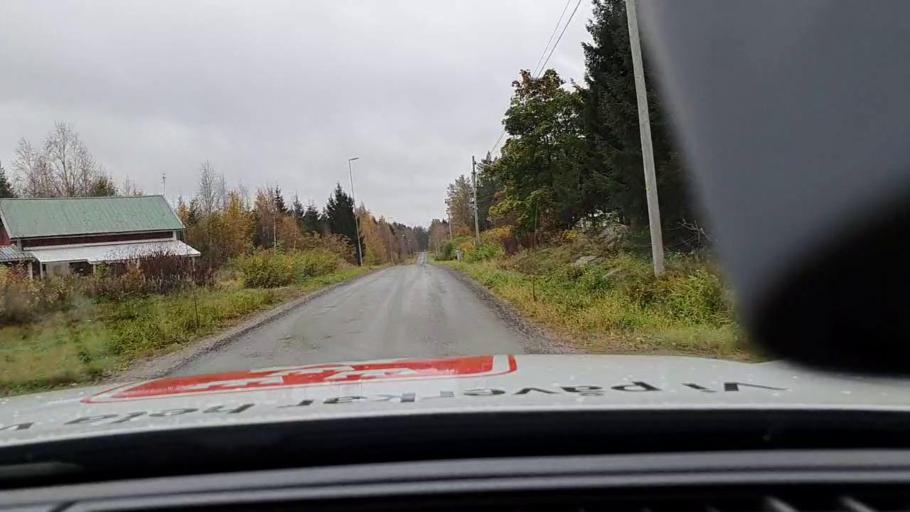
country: FI
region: Lapland
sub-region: Kemi-Tornio
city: Tornio
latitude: 65.9772
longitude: 24.0188
